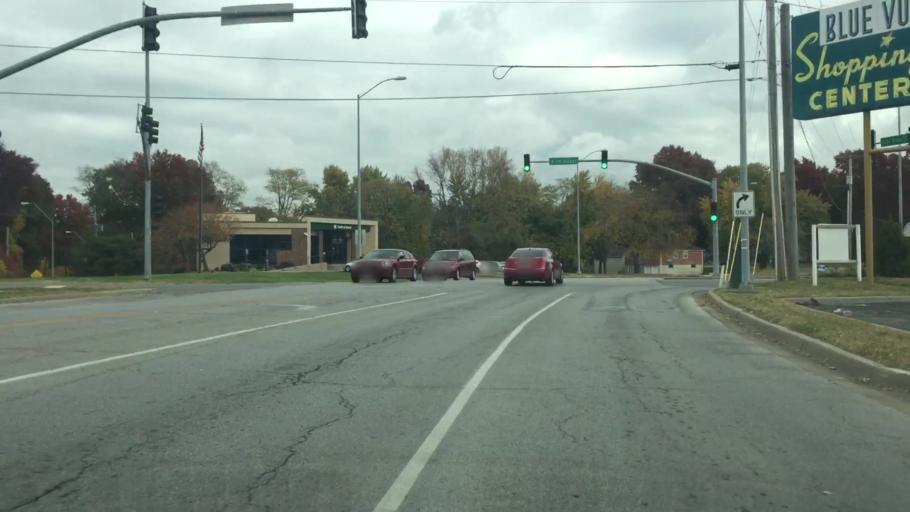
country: US
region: Missouri
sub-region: Jackson County
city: Raytown
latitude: 39.0363
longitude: -94.4387
